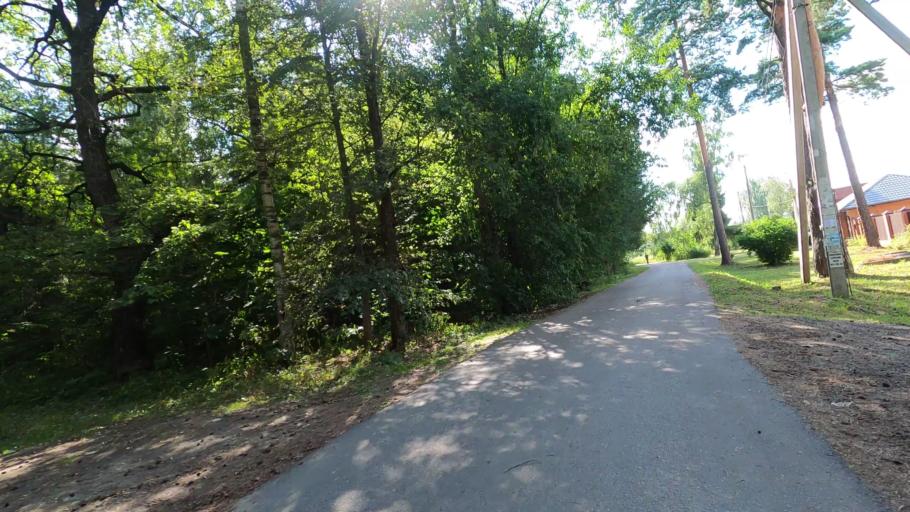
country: RU
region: Moskovskaya
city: Peski
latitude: 55.2153
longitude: 38.7563
